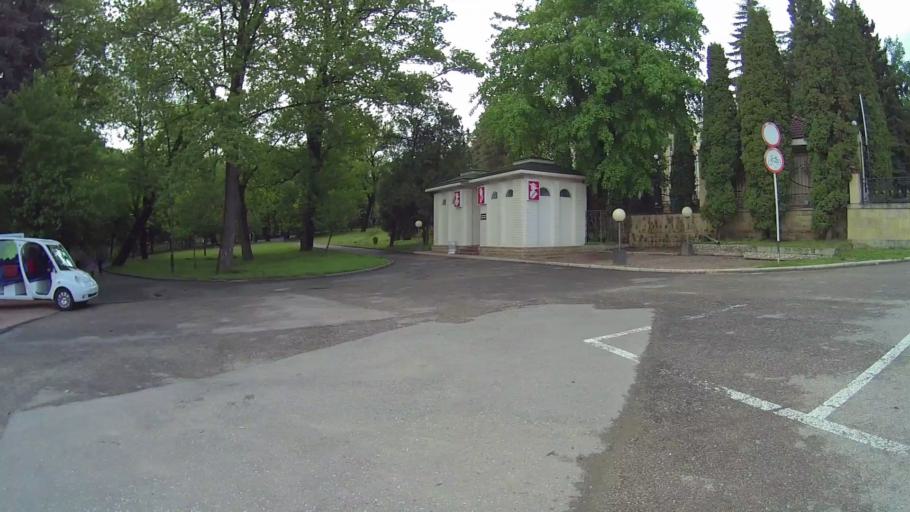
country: RU
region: Stavropol'skiy
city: Kislovodsk
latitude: 43.8983
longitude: 42.7166
